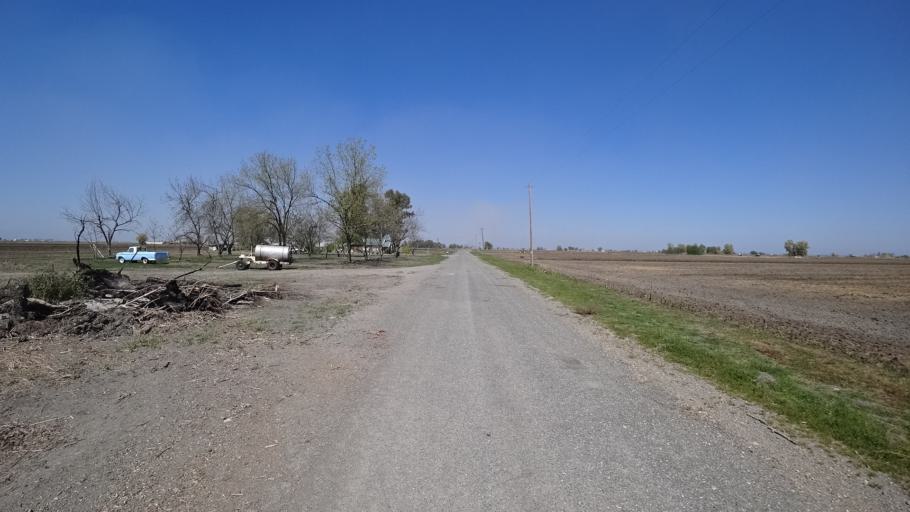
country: US
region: California
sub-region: Glenn County
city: Willows
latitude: 39.5319
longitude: -122.0981
